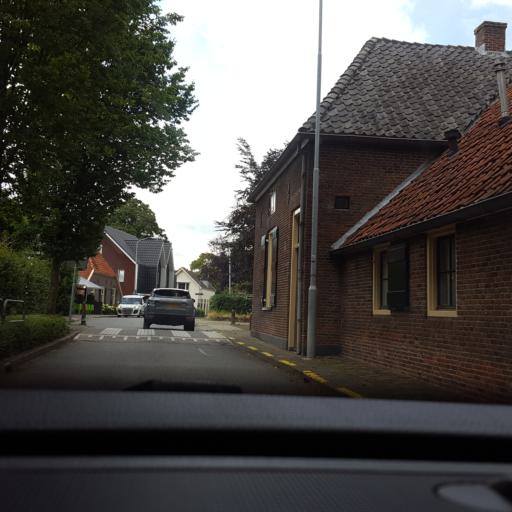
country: NL
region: Gelderland
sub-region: Gemeente Brummen
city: Brummen
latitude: 52.0632
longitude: 6.1861
